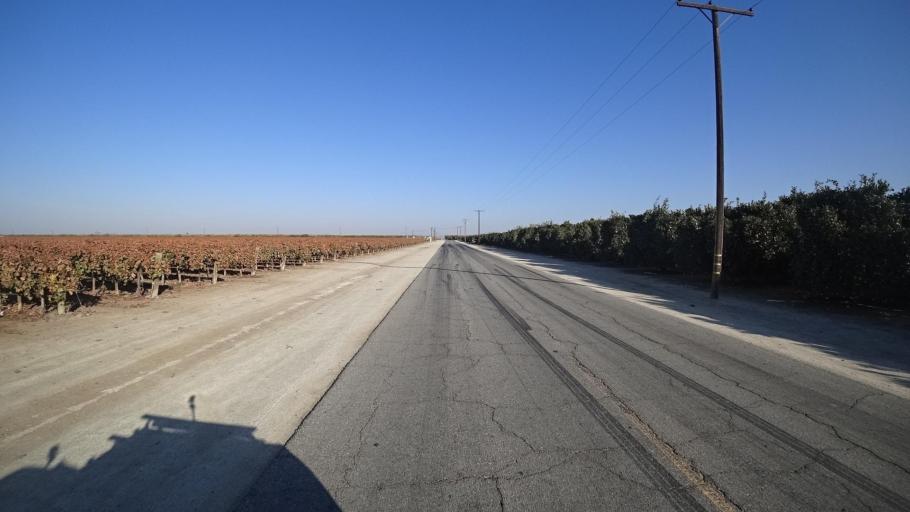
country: US
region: California
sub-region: Tulare County
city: Richgrove
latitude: 35.7875
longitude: -119.1698
